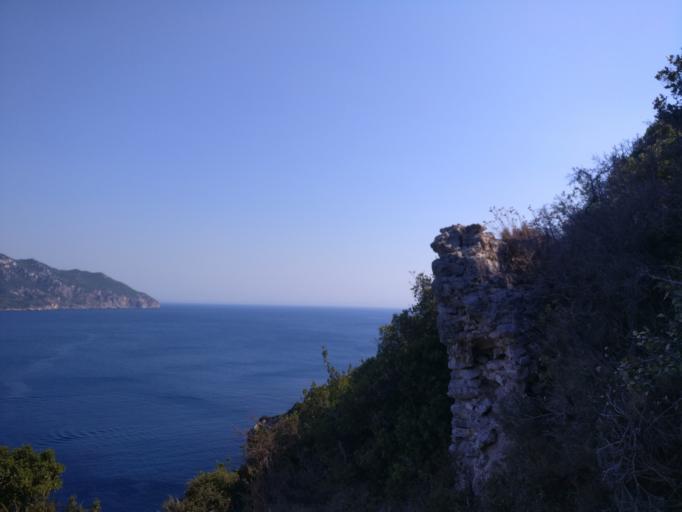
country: GR
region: Ionian Islands
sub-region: Nomos Kerkyras
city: Agios Georgis
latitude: 39.7165
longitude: 19.6589
